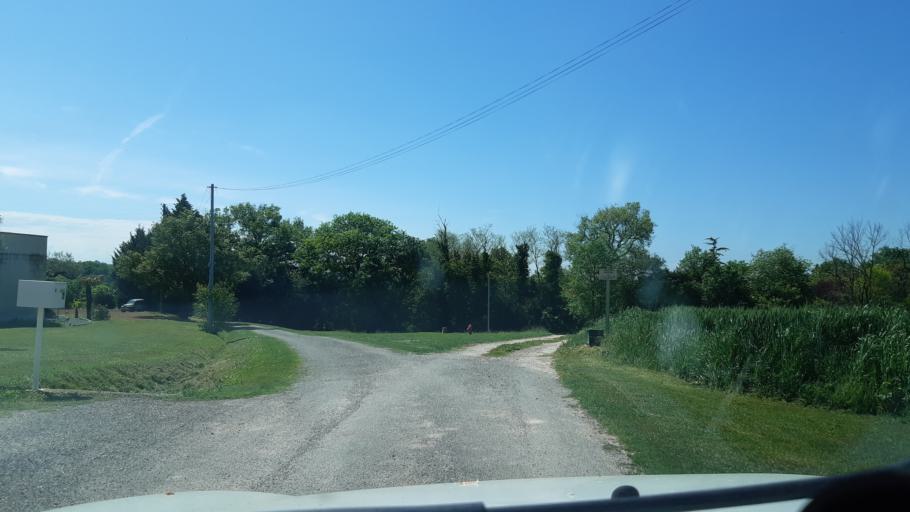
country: FR
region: Midi-Pyrenees
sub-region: Departement du Gers
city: Samatan
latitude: 43.5065
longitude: 1.0056
